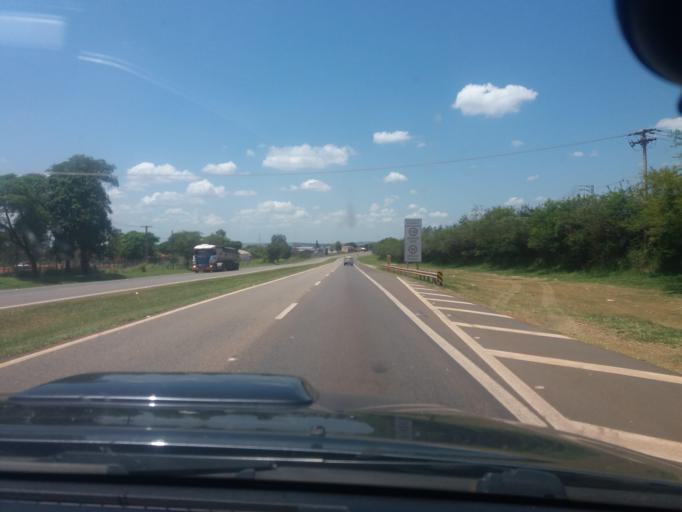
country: BR
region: Sao Paulo
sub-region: Tatui
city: Tatui
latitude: -23.3529
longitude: -47.8799
